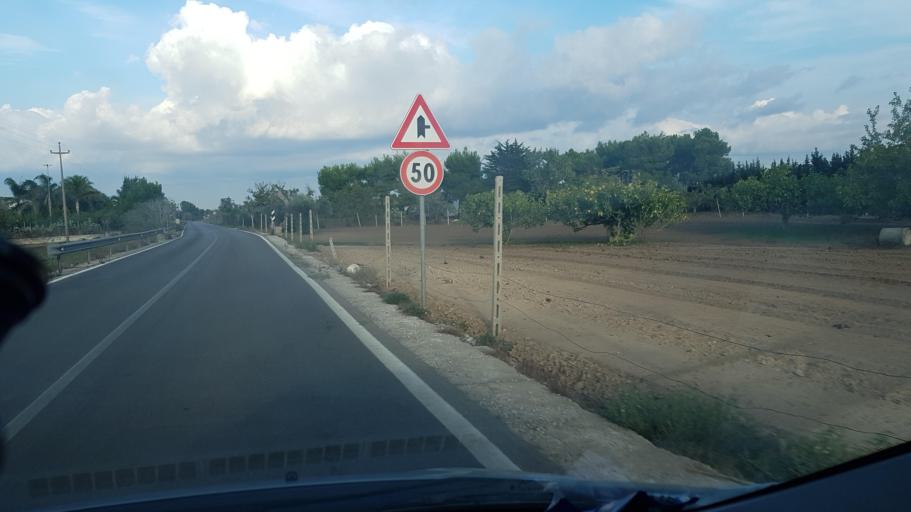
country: IT
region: Apulia
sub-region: Provincia di Lecce
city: Carmiano
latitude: 40.3420
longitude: 18.0131
